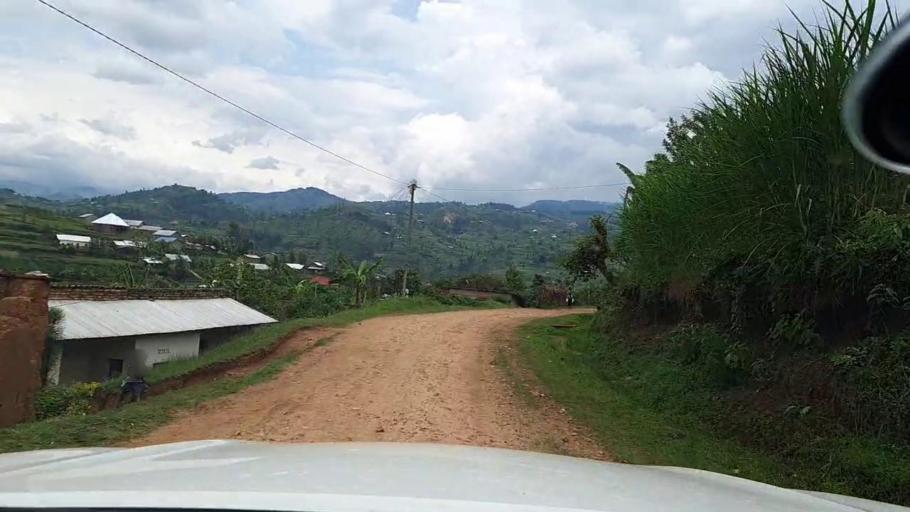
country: RW
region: Western Province
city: Kibuye
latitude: -2.0725
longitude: 29.4243
